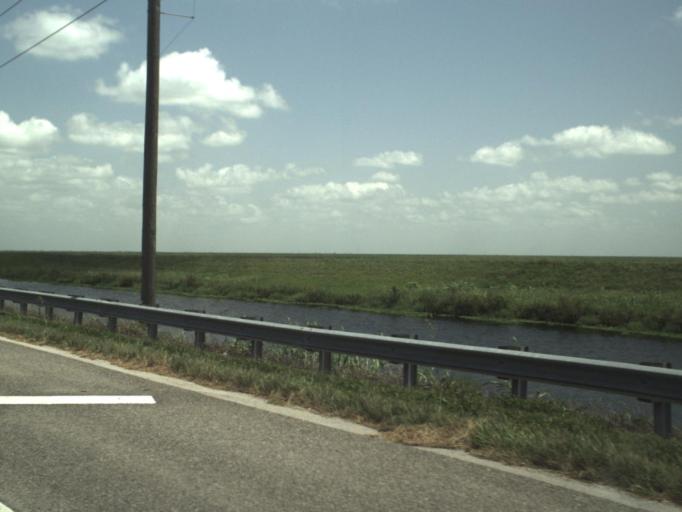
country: US
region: Florida
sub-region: Palm Beach County
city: Belle Glade Camp
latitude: 26.5826
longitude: -80.7108
